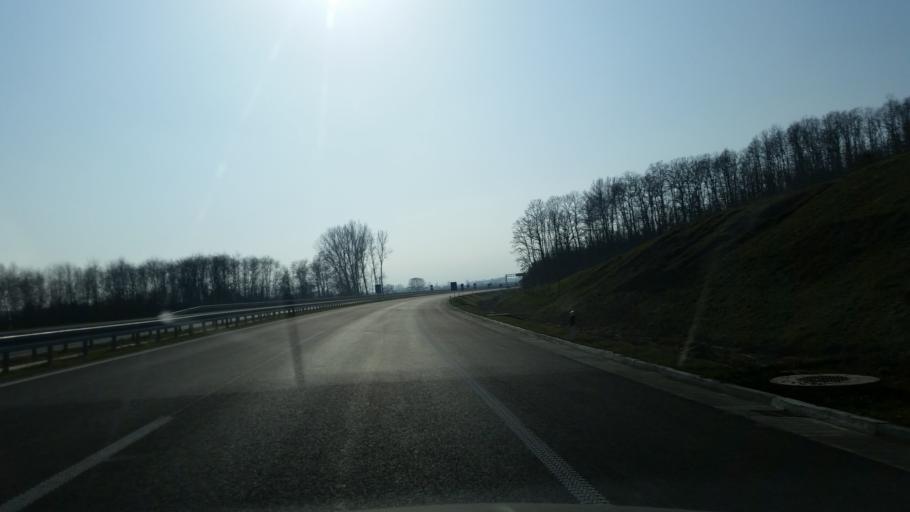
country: RS
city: Prislonica
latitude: 43.9291
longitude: 20.4017
